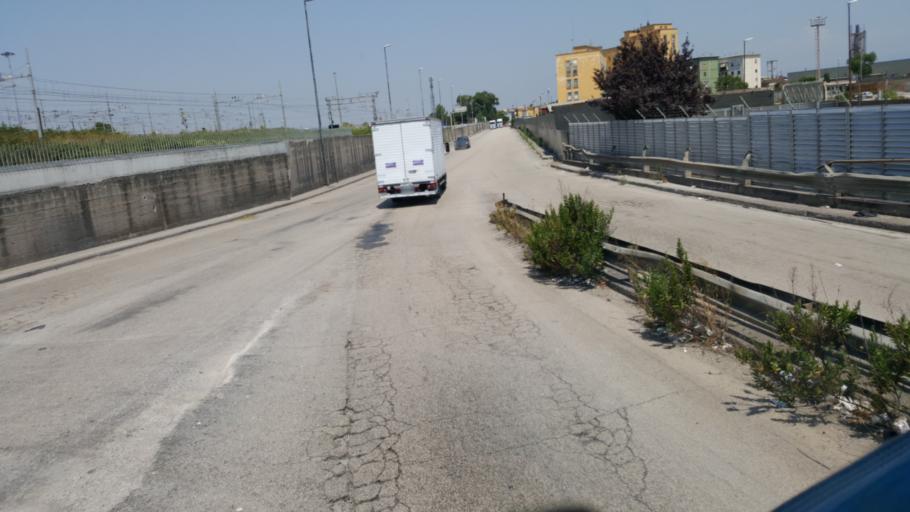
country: IT
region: Campania
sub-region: Provincia di Napoli
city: San Giorgio a Cremano
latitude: 40.8482
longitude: 14.2977
